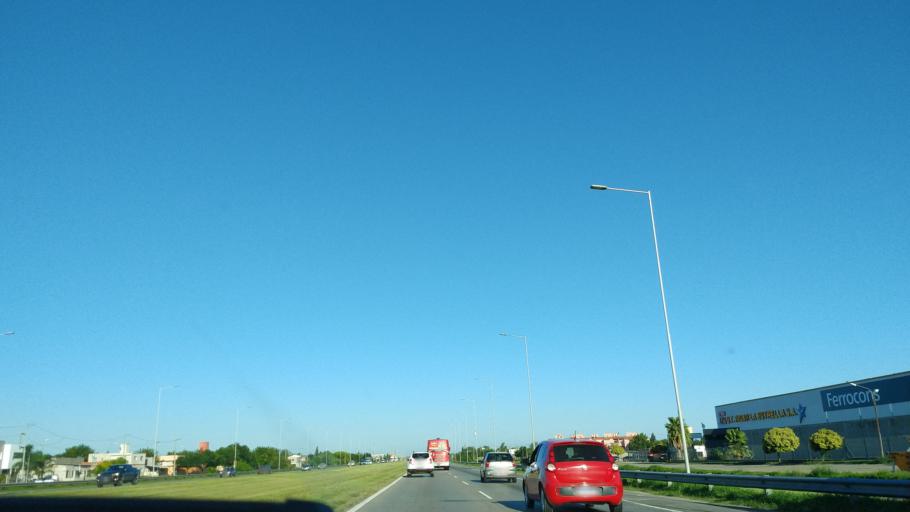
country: AR
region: Cordoba
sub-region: Departamento de Capital
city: Cordoba
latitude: -31.3597
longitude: -64.1644
